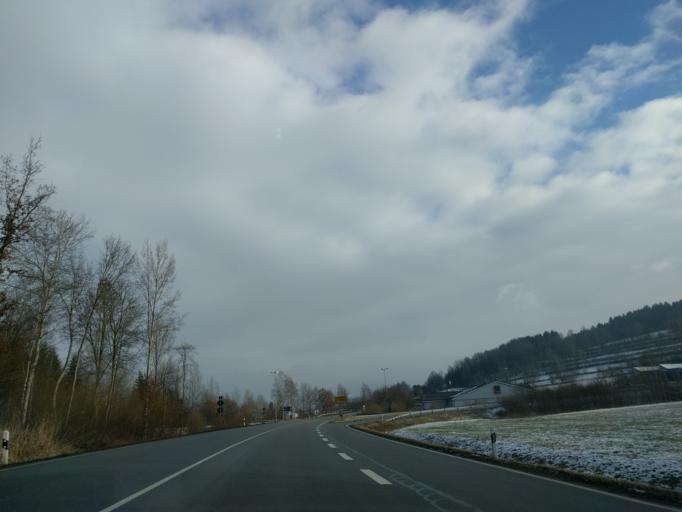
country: DE
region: Bavaria
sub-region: Lower Bavaria
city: Zwiesel
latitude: 49.0004
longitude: 13.2165
